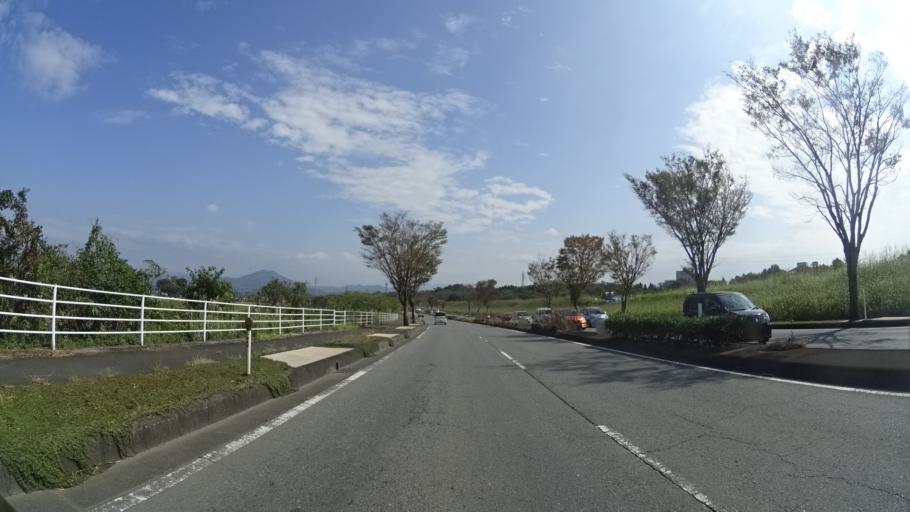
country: JP
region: Kumamoto
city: Kumamoto
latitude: 32.7336
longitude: 130.7571
